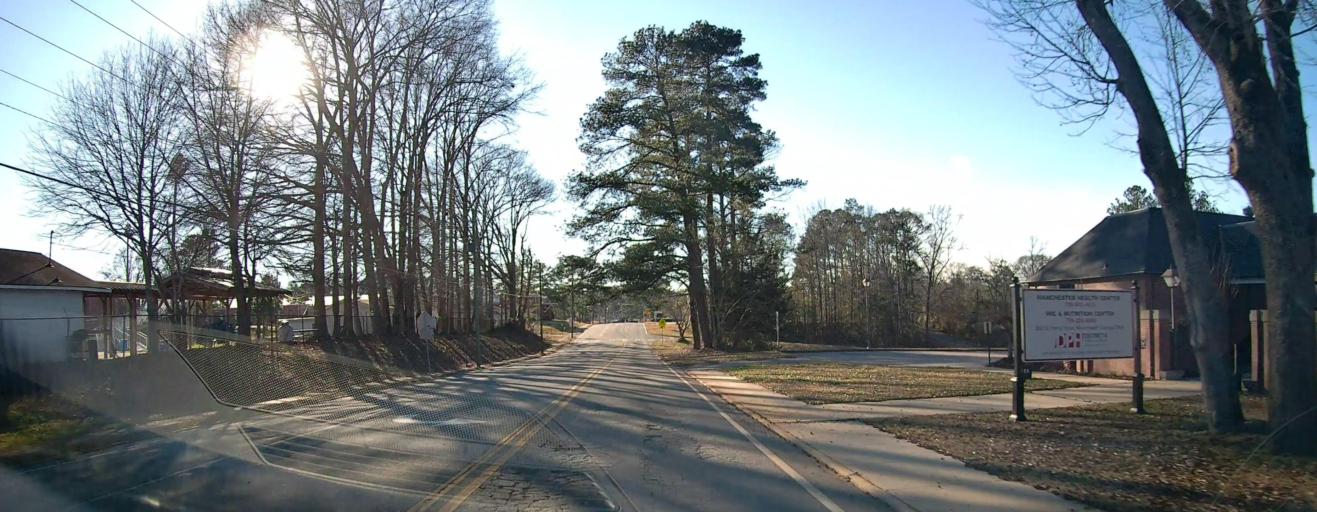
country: US
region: Georgia
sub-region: Meriwether County
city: Manchester
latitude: 32.8601
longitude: -84.6170
